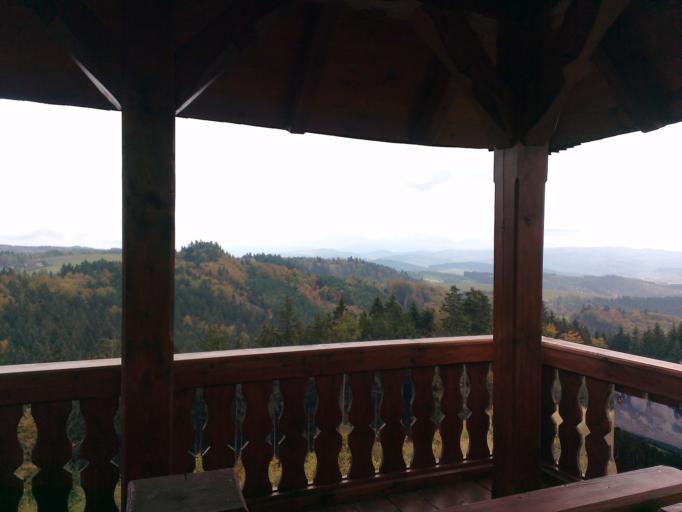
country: CZ
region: Zlin
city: Host'alkova
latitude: 49.3659
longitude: 17.8284
